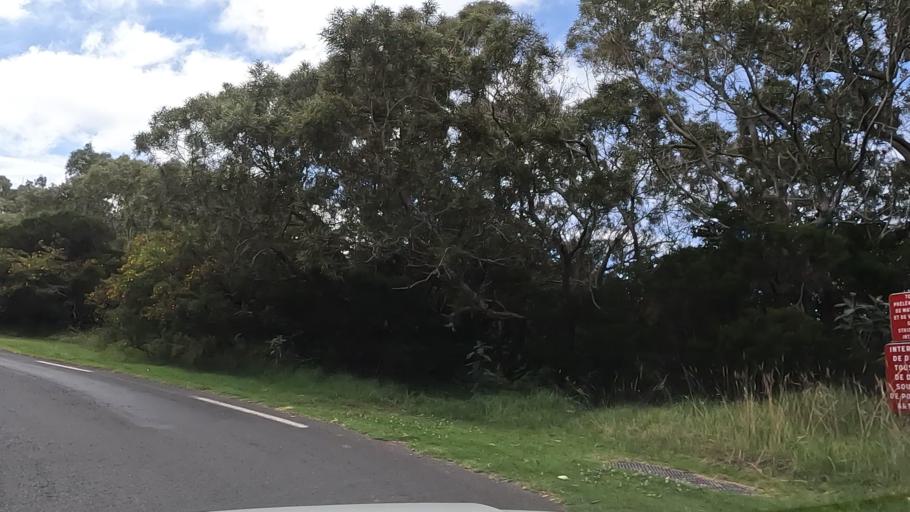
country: RE
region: Reunion
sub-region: Reunion
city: Le Tampon
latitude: -21.2418
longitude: 55.5857
